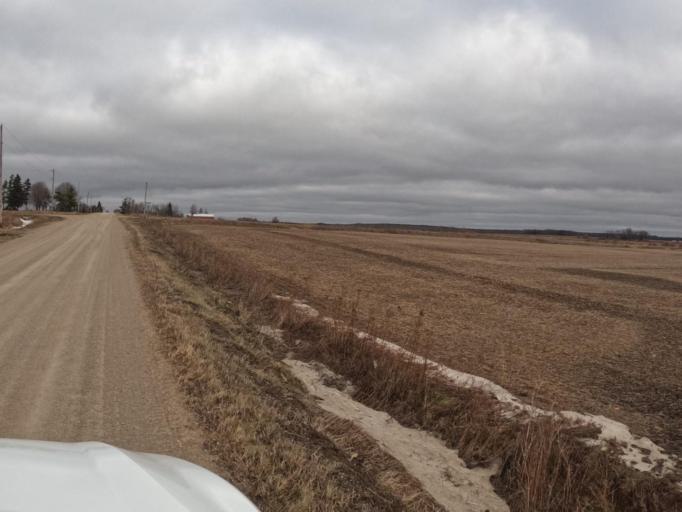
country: CA
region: Ontario
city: Shelburne
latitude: 44.0055
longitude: -80.4106
